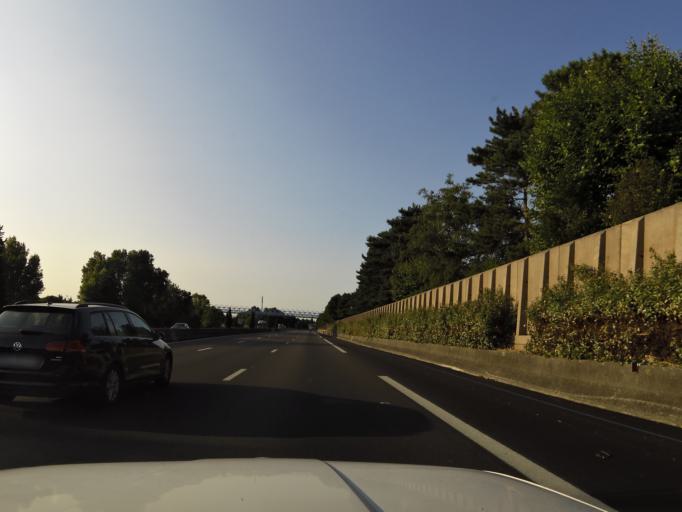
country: FR
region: Rhone-Alpes
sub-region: Departement de la Drome
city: Valence
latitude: 44.9385
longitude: 4.8897
